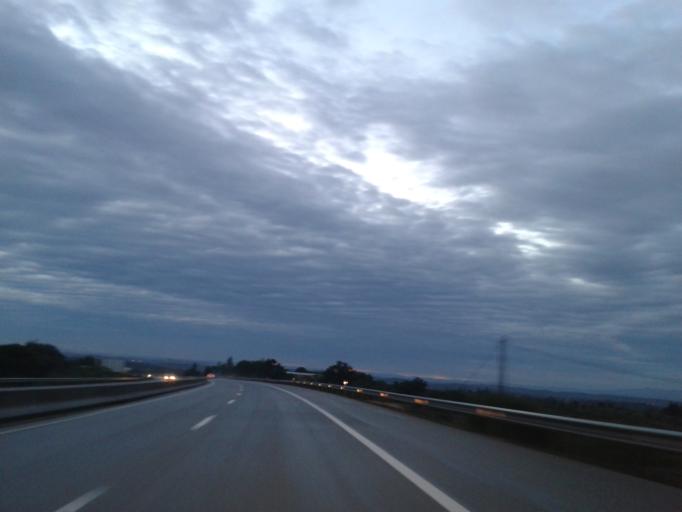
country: PT
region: Faro
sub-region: Lagoa
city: Estombar
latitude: 37.1571
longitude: -8.4672
